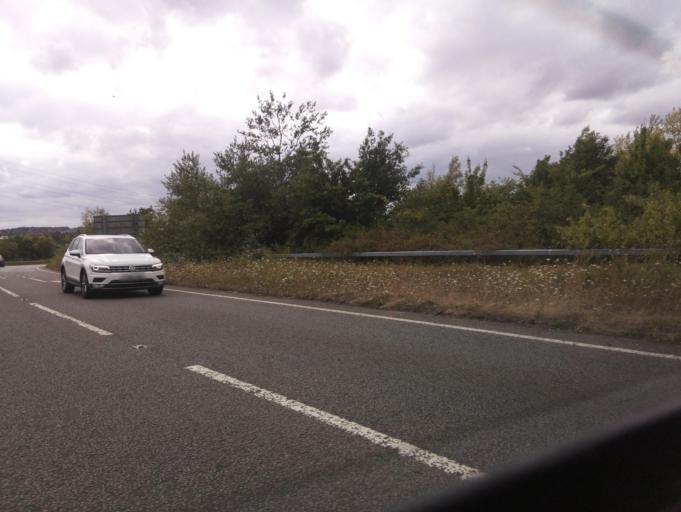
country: GB
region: England
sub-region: Leicestershire
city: Castle Donington
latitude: 52.8596
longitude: -1.3274
